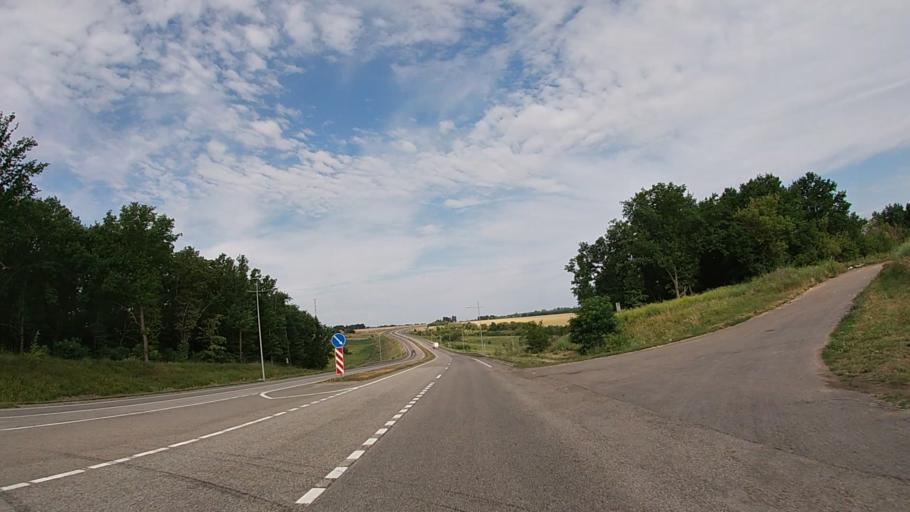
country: RU
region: Belgorod
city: Tomarovka
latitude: 50.7070
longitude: 36.2078
